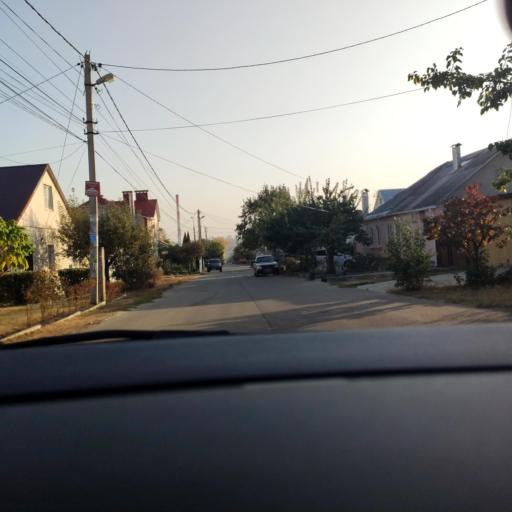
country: RU
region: Voronezj
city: Podgornoye
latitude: 51.6977
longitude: 39.1532
